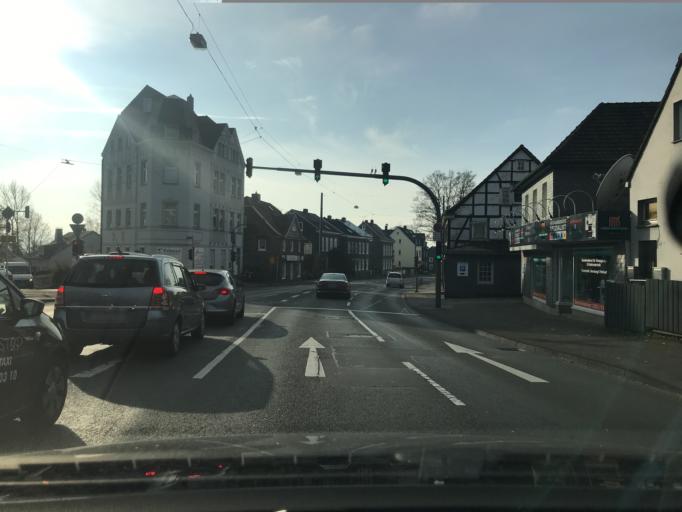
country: DE
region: North Rhine-Westphalia
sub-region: Regierungsbezirk Dusseldorf
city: Wuppertal
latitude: 51.2173
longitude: 7.1501
